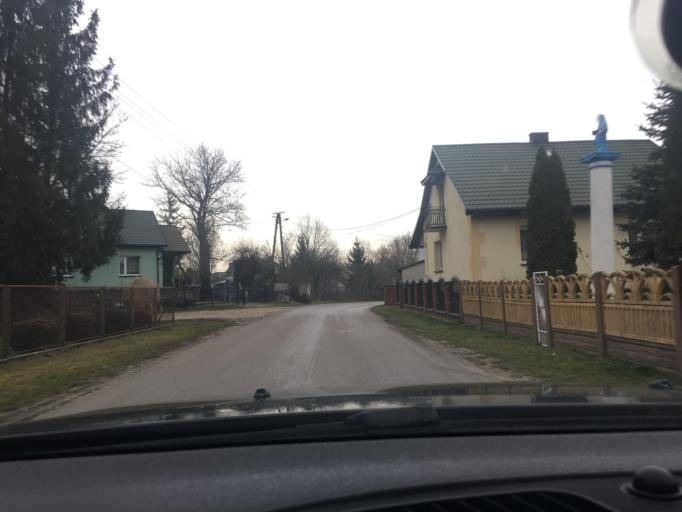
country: PL
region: Swietokrzyskie
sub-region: Powiat jedrzejowski
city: Imielno
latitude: 50.6352
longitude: 20.4118
